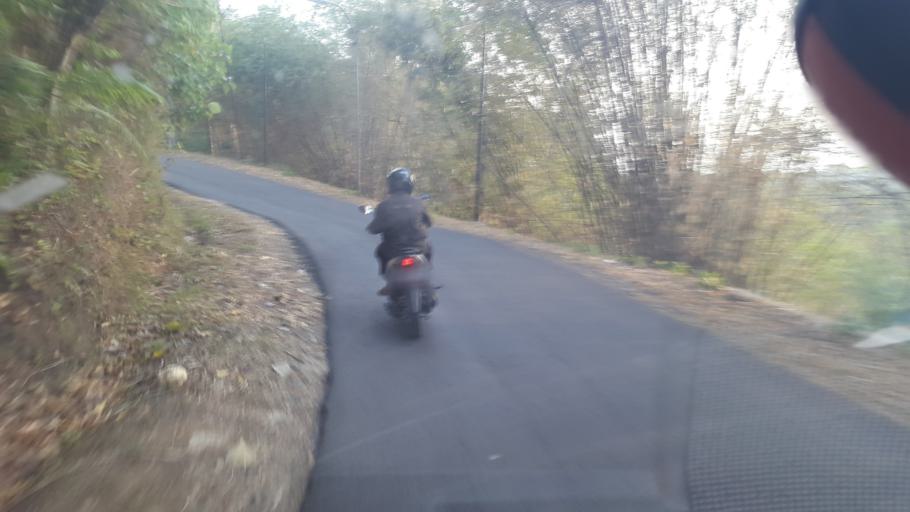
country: ID
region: West Java
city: Pondokaso
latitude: -7.3504
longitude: 106.5338
